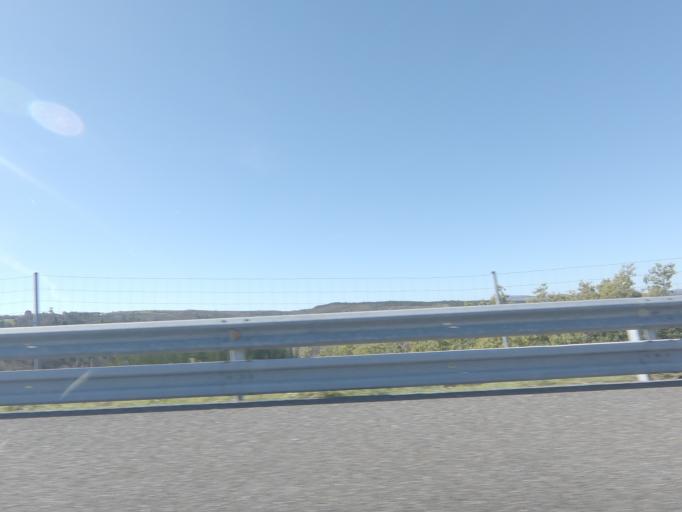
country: ES
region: Galicia
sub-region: Provincia de Pontevedra
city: Dozon
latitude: 42.5705
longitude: -8.0600
